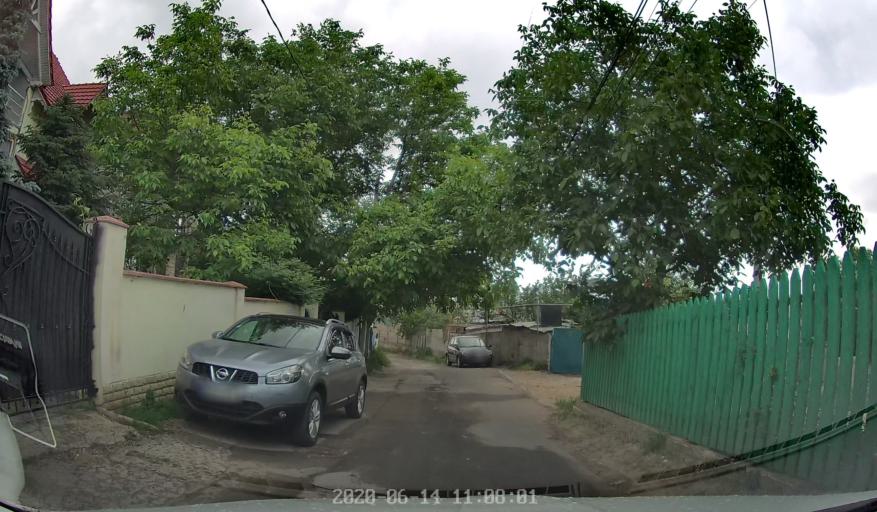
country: MD
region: Chisinau
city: Chisinau
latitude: 47.0441
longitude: 28.8380
